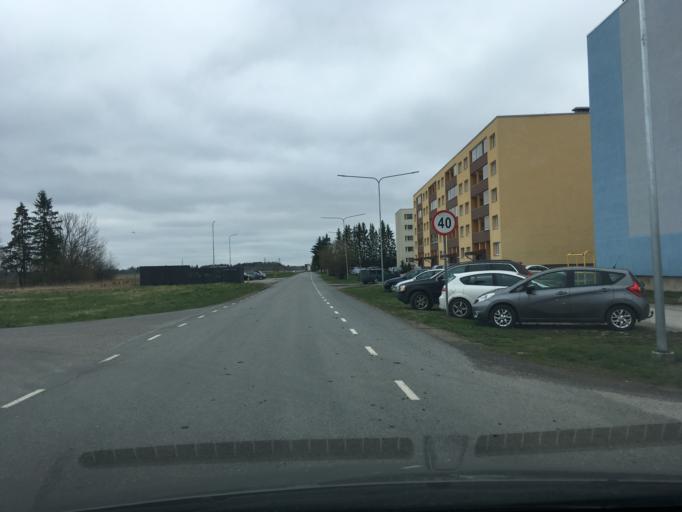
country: EE
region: Harju
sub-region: Rae vald
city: Vaida
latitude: 59.2886
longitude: 24.9798
